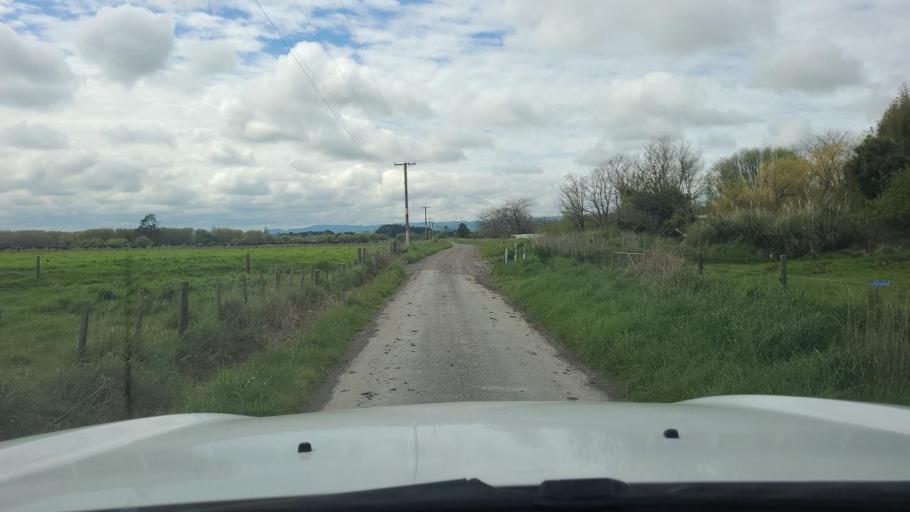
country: NZ
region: Wellington
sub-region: Masterton District
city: Masterton
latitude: -41.0958
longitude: 175.4950
